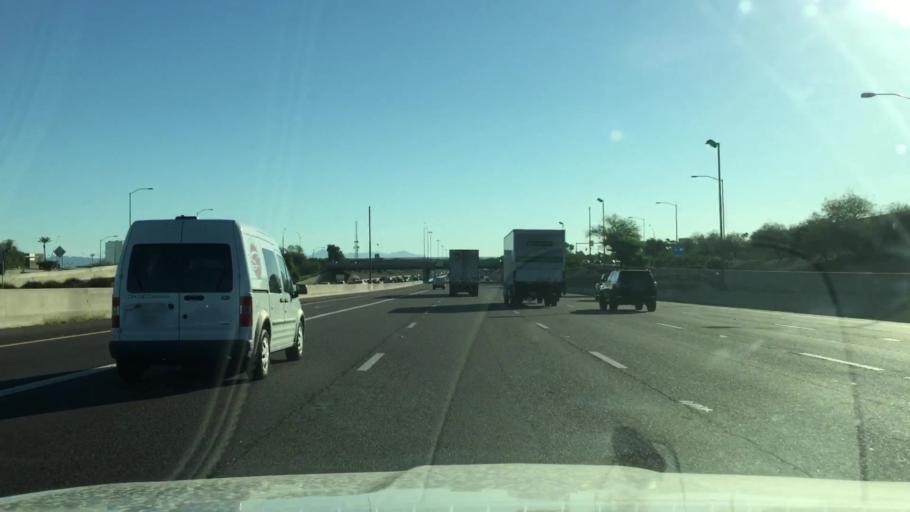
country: US
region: Arizona
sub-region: Maricopa County
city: Tempe
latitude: 33.3854
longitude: -111.8784
